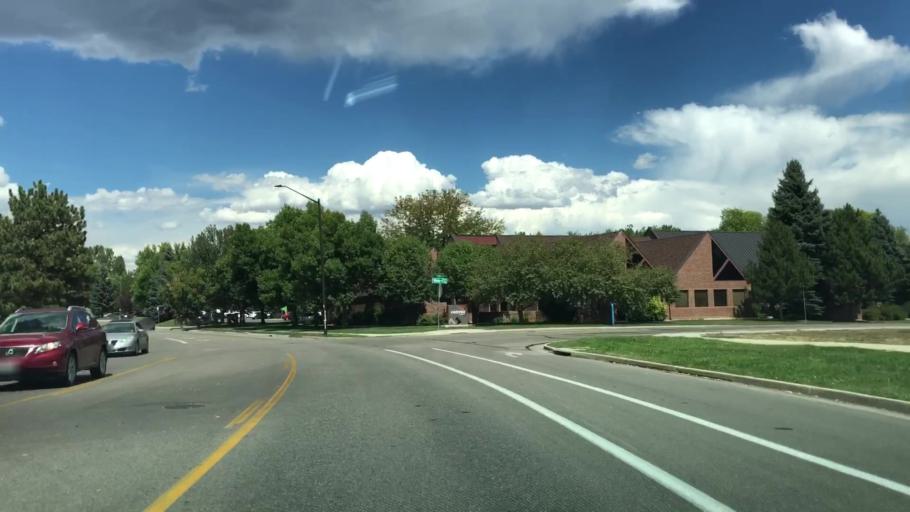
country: US
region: Colorado
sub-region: Larimer County
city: Fort Collins
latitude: 40.5250
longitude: -105.0653
